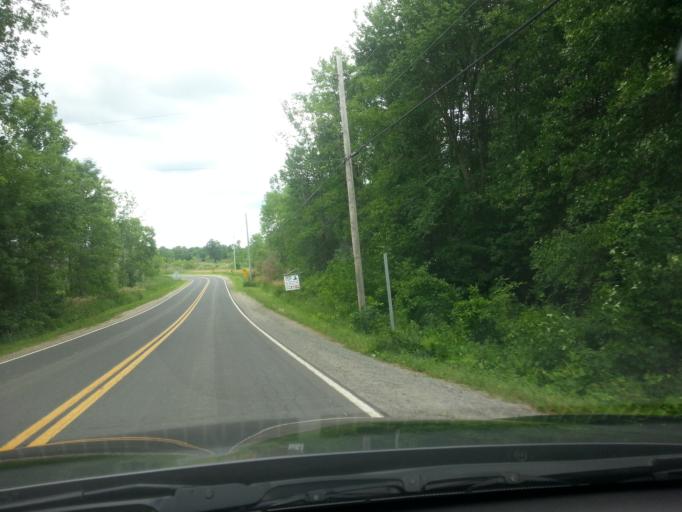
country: CA
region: Ontario
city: Perth
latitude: 44.6553
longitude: -76.2584
